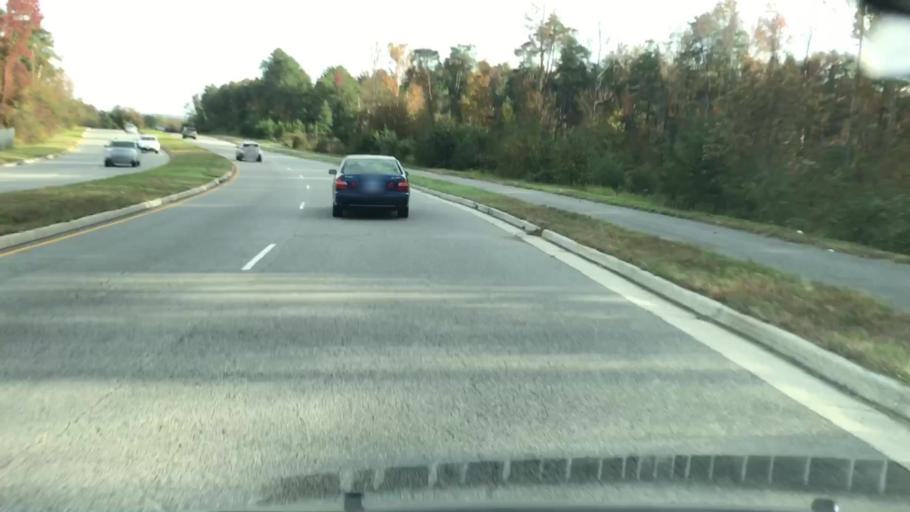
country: US
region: Virginia
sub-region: Fairfax County
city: Woodlawn
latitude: 38.7285
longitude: -77.1416
